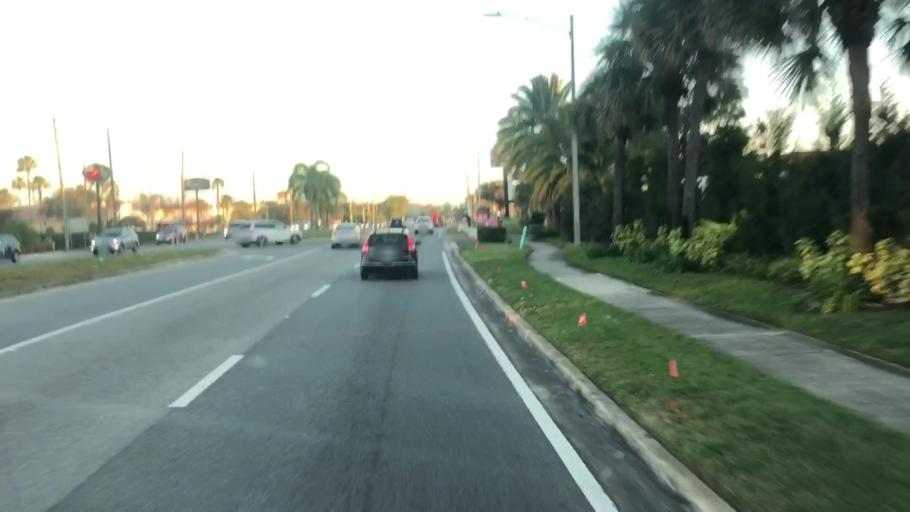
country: US
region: Florida
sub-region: Orange County
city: Doctor Phillips
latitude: 28.3871
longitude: -81.5062
